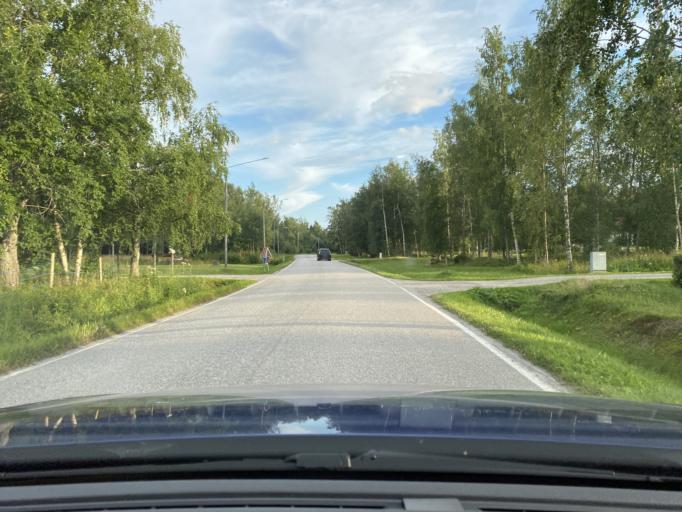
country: FI
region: Ostrobothnia
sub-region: Vaasa
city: Korsnaes
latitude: 62.9615
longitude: 21.1883
